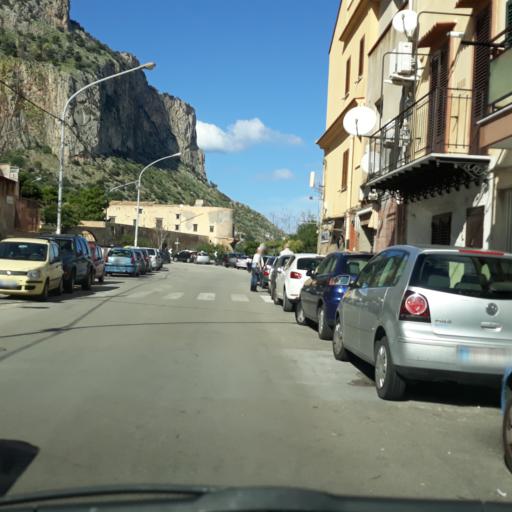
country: IT
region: Sicily
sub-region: Palermo
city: Palermo
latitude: 38.1646
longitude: 13.3694
